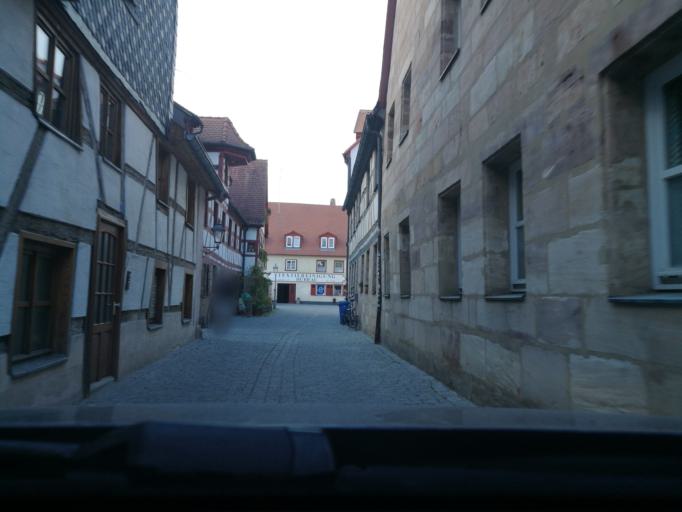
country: DE
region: Bavaria
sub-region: Regierungsbezirk Mittelfranken
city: Furth
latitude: 49.4805
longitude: 10.9850
